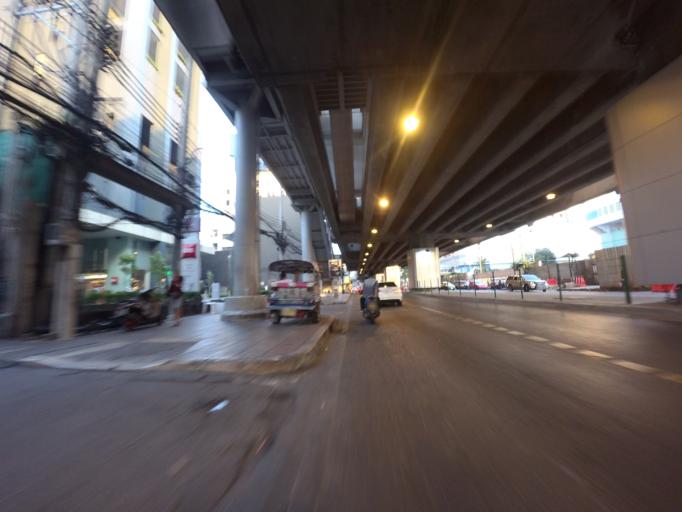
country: TH
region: Bangkok
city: Pathum Wan
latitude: 13.7467
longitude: 100.5286
